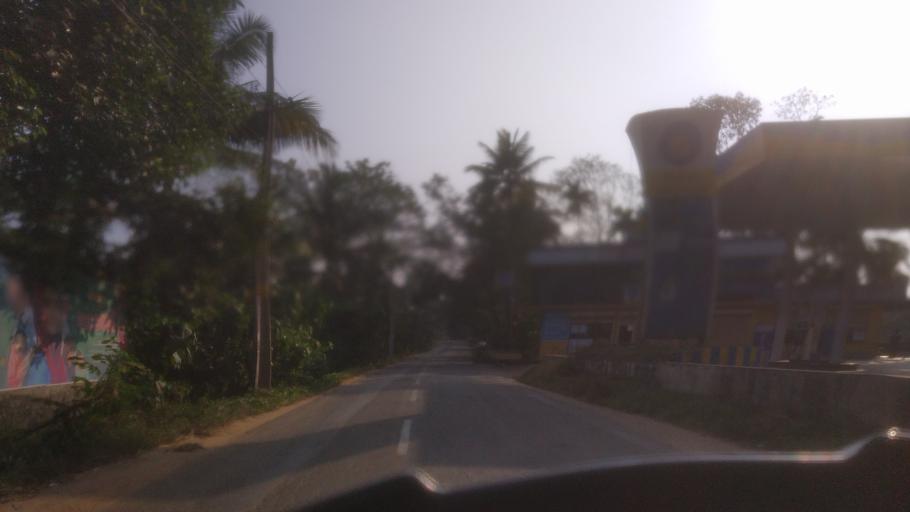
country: IN
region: Kerala
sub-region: Ernakulam
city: Piravam
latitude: 9.8196
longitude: 76.5023
